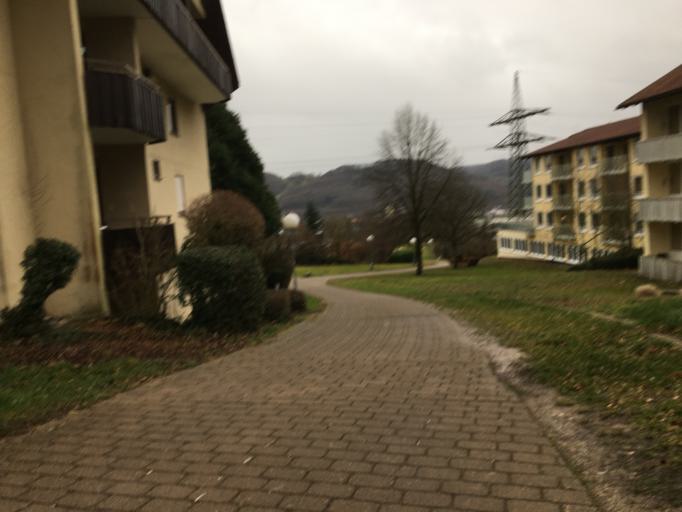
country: DE
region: Baden-Wuerttemberg
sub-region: Freiburg Region
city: Bad Sackingen
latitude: 47.5623
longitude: 7.9398
